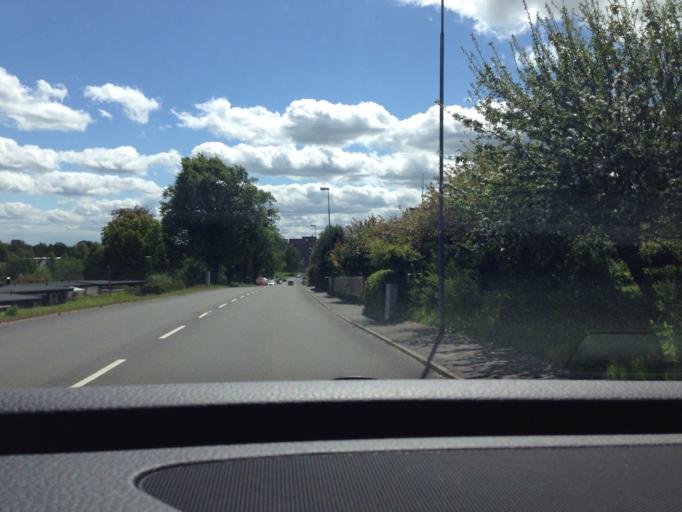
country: SE
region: Vaestra Goetaland
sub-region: Skovde Kommun
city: Skoevde
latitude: 58.4049
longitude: 13.8334
